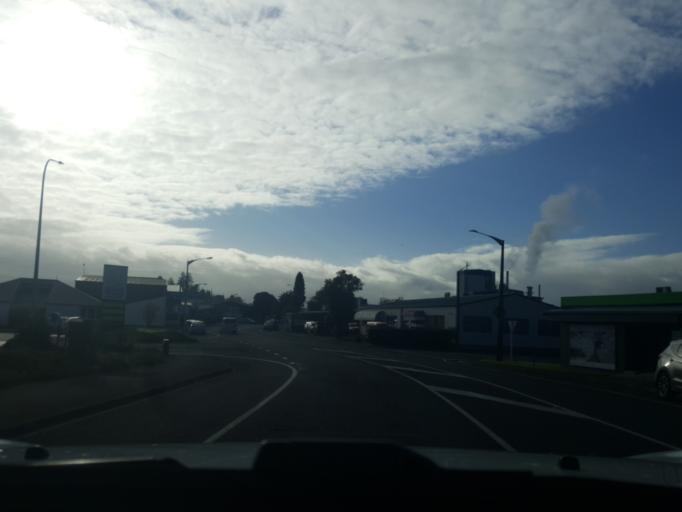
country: NZ
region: Waikato
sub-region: Waipa District
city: Cambridge
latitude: -37.6590
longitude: 175.5297
